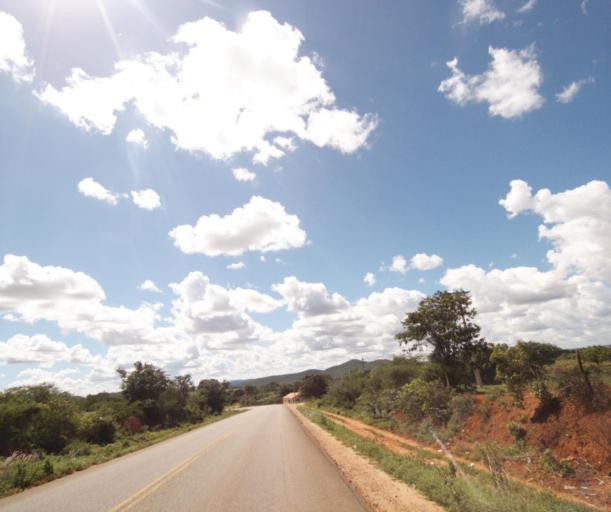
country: BR
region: Bahia
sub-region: Caetite
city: Caetite
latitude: -14.1722
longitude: -42.1861
